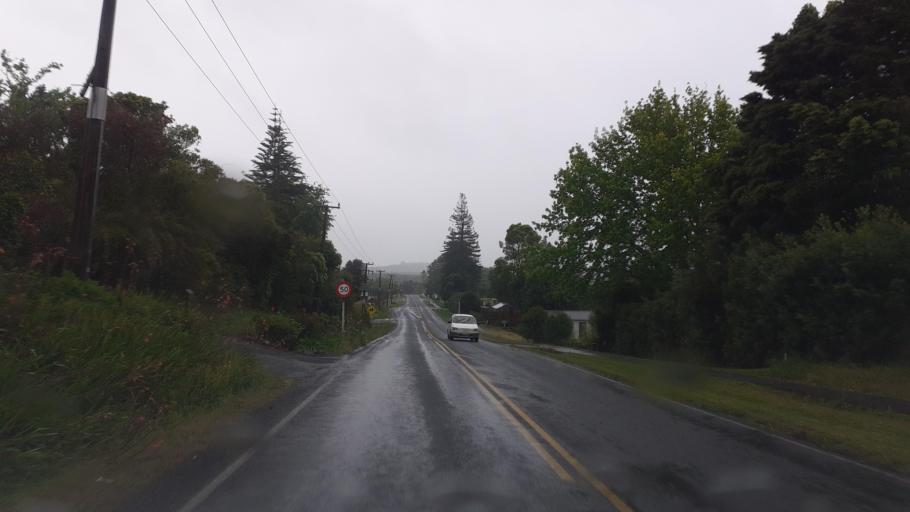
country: NZ
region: Northland
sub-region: Far North District
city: Kerikeri
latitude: -35.2107
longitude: 173.9625
